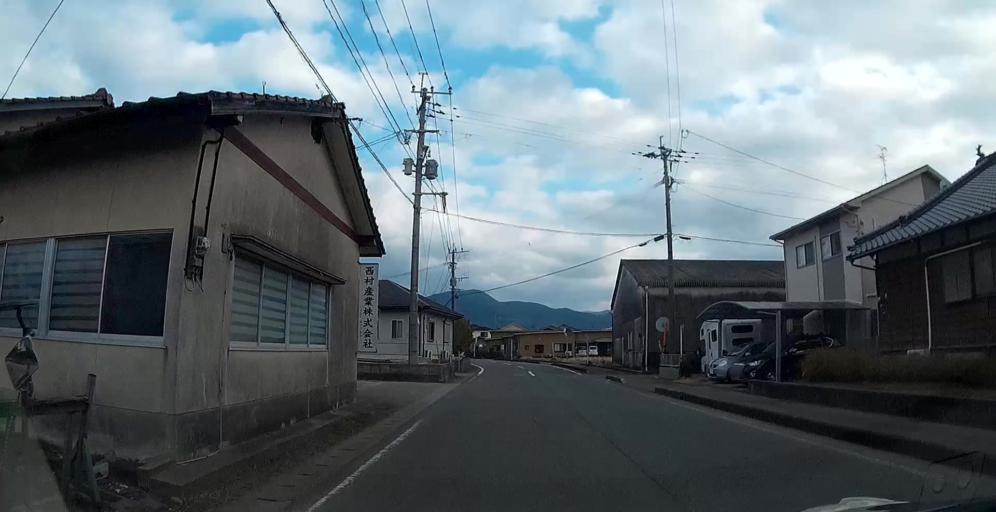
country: JP
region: Kumamoto
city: Yatsushiro
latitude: 32.5391
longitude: 130.6271
